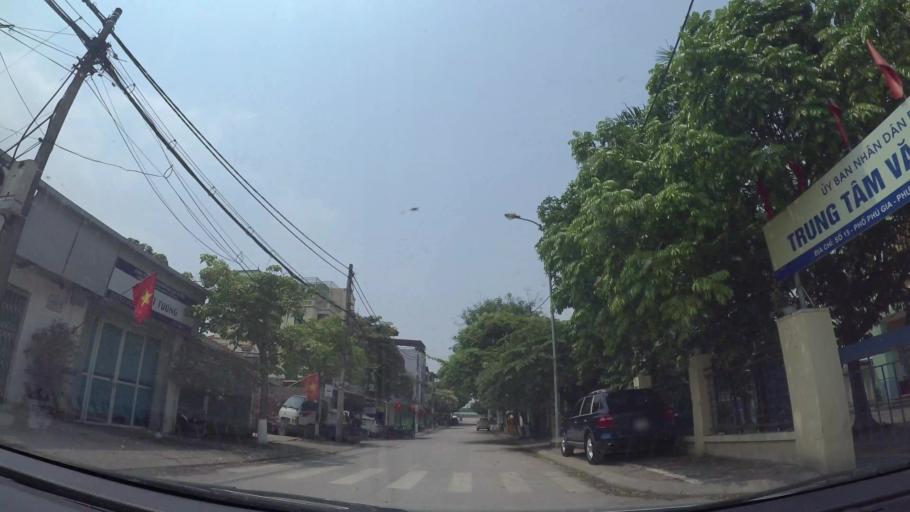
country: VN
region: Ha Noi
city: Tay Ho
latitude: 21.0887
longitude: 105.8087
